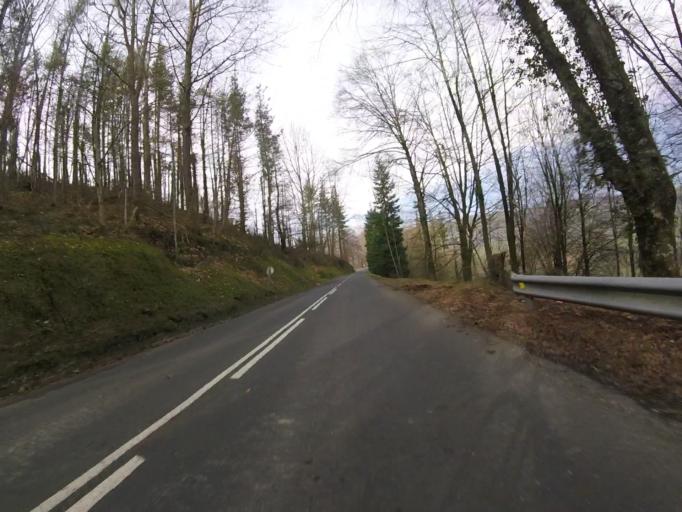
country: ES
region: Basque Country
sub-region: Provincia de Guipuzcoa
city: Beizama
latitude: 43.1641
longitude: -2.2138
